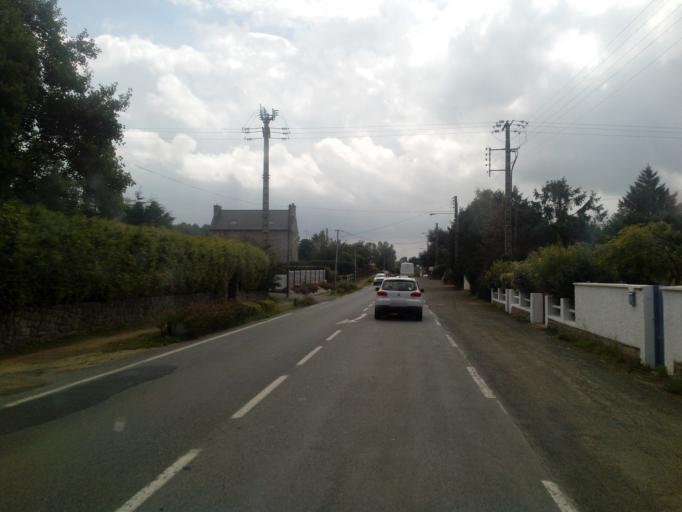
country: FR
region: Brittany
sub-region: Departement des Cotes-d'Armor
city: Plouha
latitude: 48.6869
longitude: -2.9309
